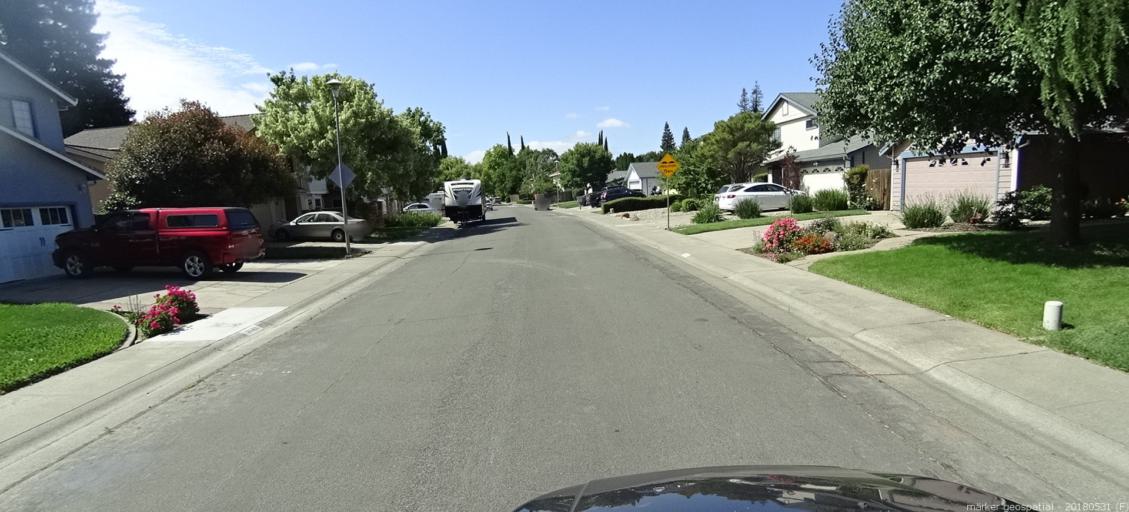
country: US
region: California
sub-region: Sacramento County
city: Sacramento
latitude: 38.6237
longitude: -121.5087
